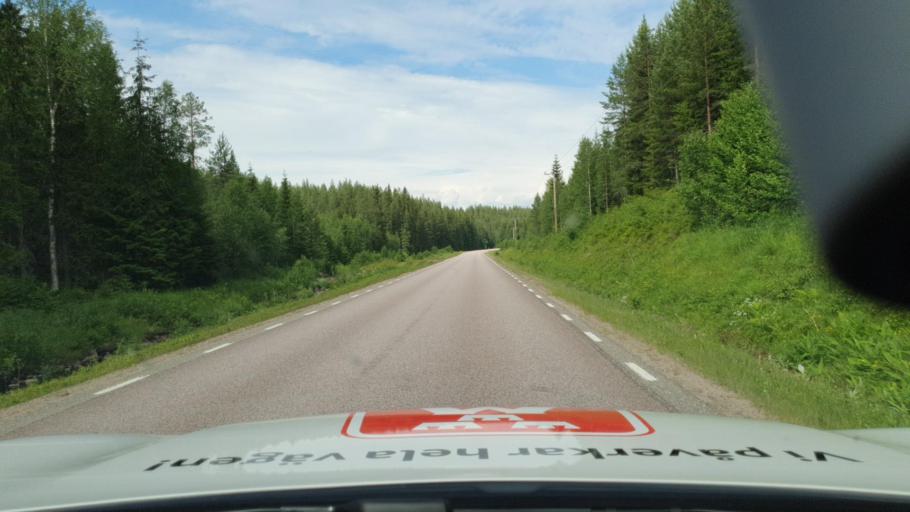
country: SE
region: Vaermland
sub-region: Torsby Kommun
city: Torsby
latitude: 60.7449
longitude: 12.7010
